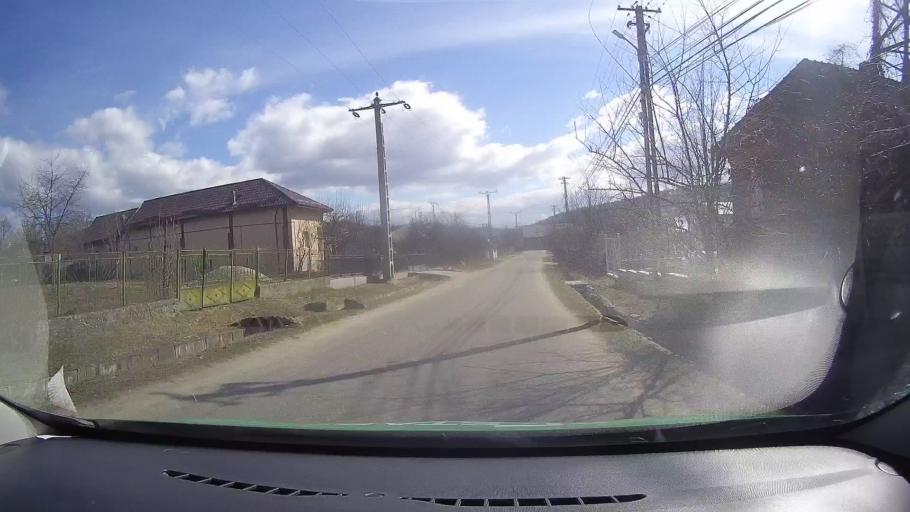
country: RO
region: Dambovita
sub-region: Comuna Branesti
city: Branesti
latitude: 45.0324
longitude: 25.4158
